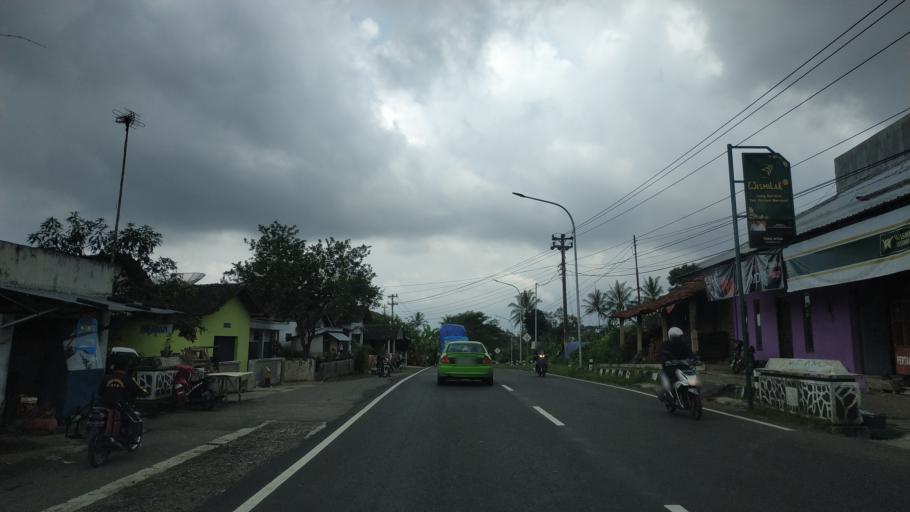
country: ID
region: Central Java
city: Magelang
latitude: -7.2887
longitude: 110.1277
